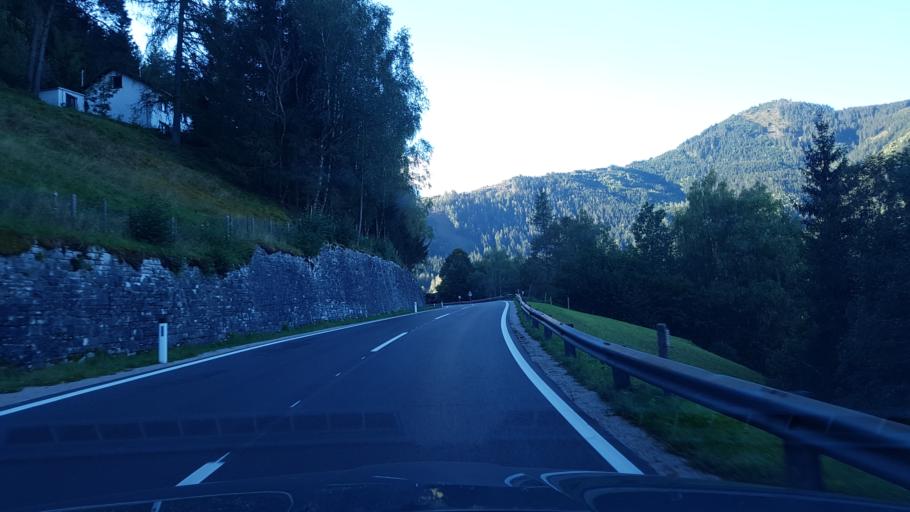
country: AT
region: Styria
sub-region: Politischer Bezirk Liezen
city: Grosssolk
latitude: 47.4205
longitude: 13.9571
